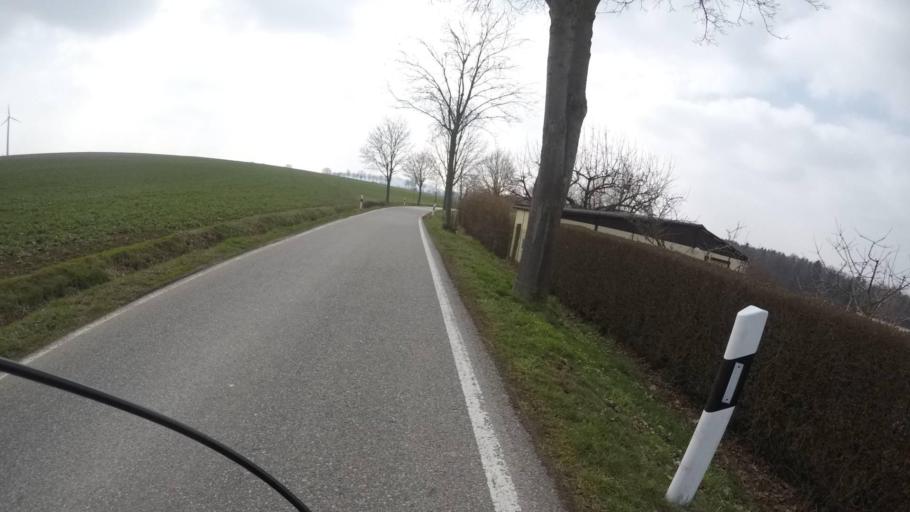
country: DE
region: Saxony
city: Niederfrohna
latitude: 50.8588
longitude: 12.7053
